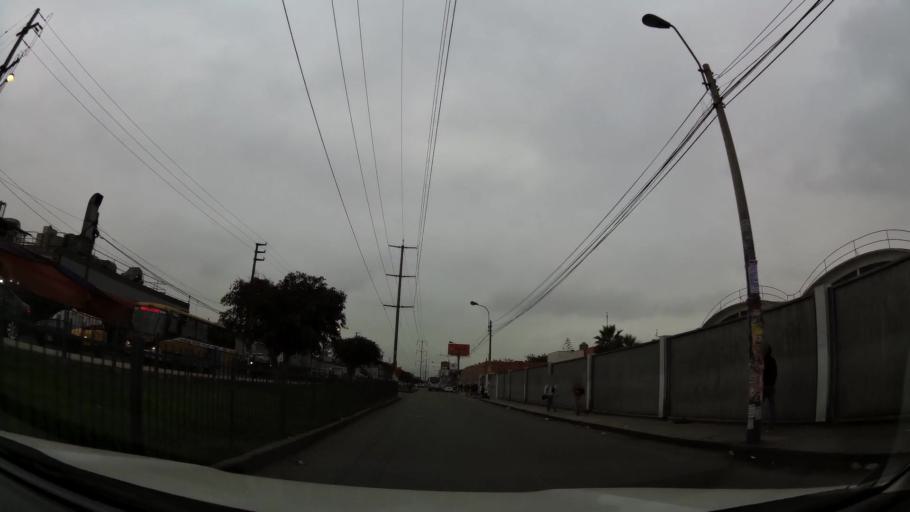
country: PE
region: Lima
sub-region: Lima
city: La Molina
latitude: -12.0557
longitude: -76.9643
